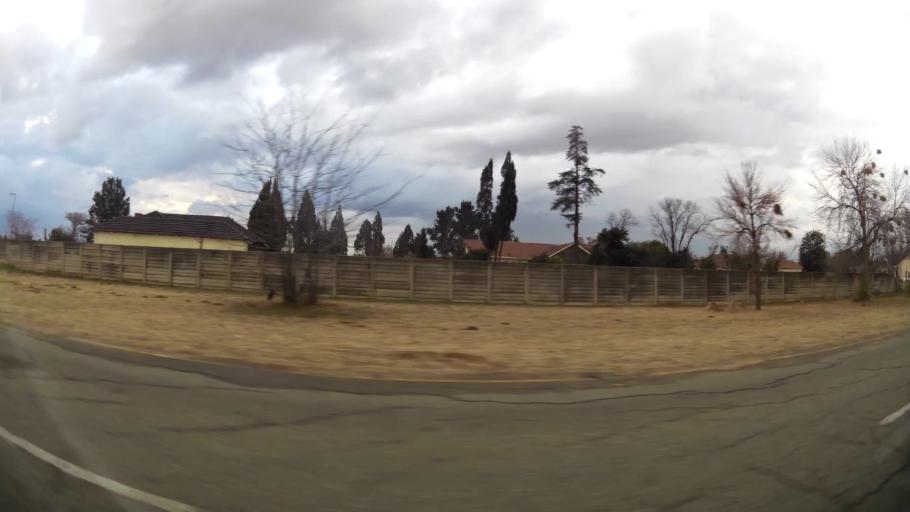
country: ZA
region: Orange Free State
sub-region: Lejweleputswa District Municipality
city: Welkom
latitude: -27.9620
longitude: 26.7196
